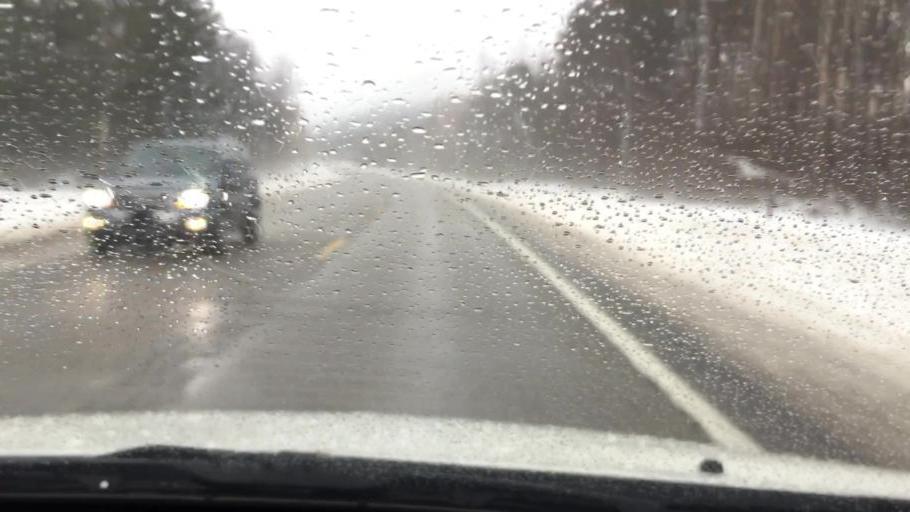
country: US
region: Michigan
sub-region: Charlevoix County
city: East Jordan
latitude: 45.1084
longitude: -85.1270
